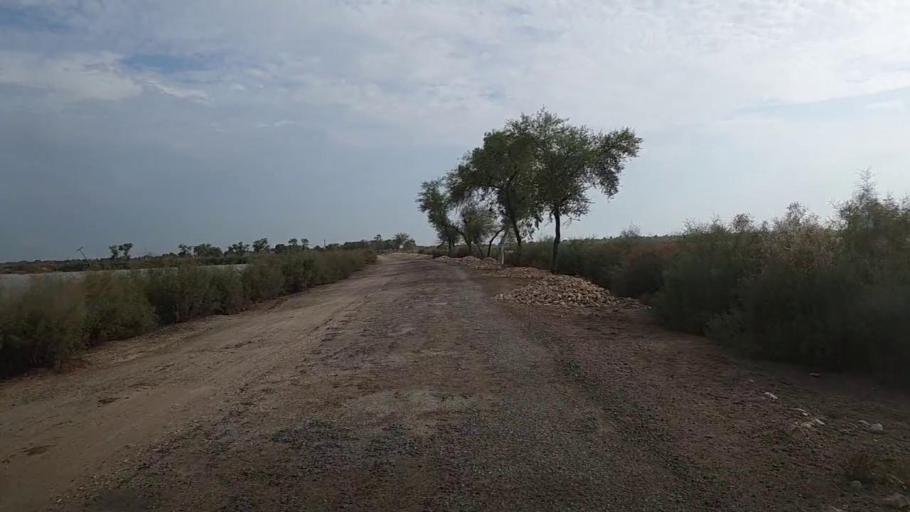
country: PK
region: Sindh
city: Thul
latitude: 28.2772
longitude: 68.8549
